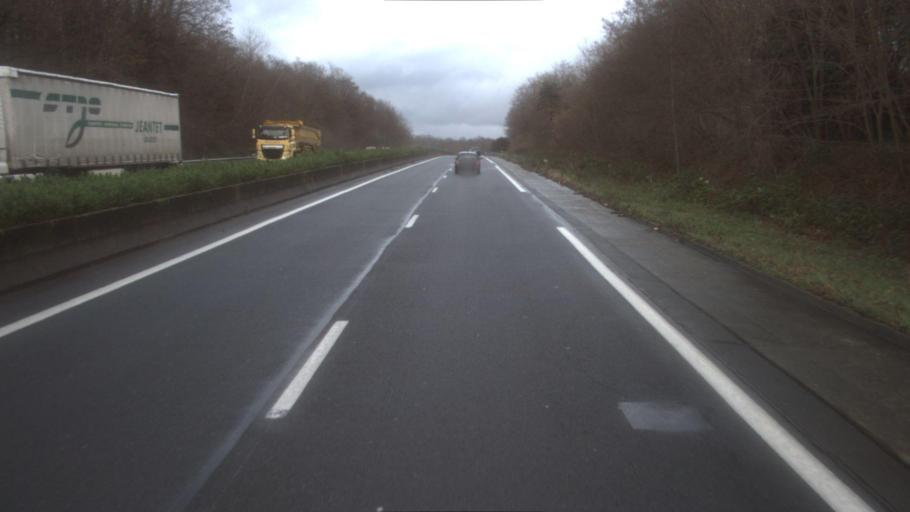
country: FR
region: Ile-de-France
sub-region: Departement de Seine-et-Marne
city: Cely
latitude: 48.4704
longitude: 2.5287
